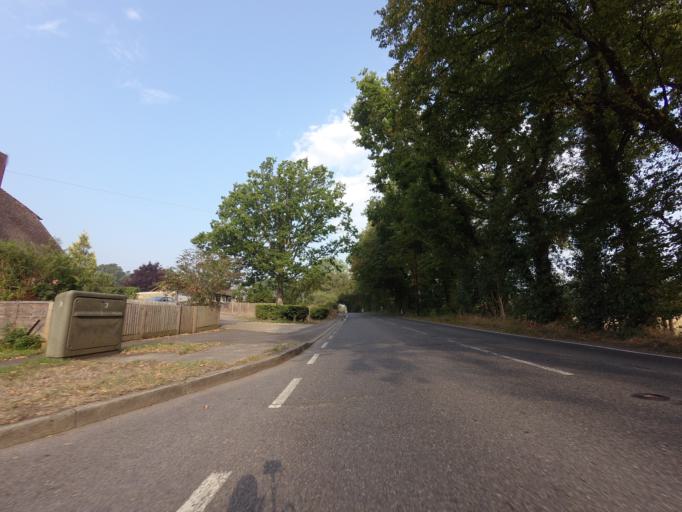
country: GB
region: England
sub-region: Kent
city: Tenterden
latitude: 51.1262
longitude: 0.7591
